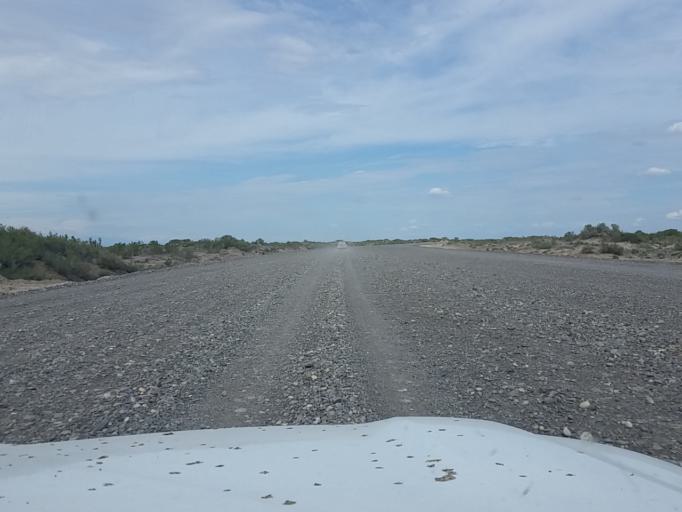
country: KZ
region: Almaty Oblysy
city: Zharkent
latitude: 43.8641
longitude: 79.3654
